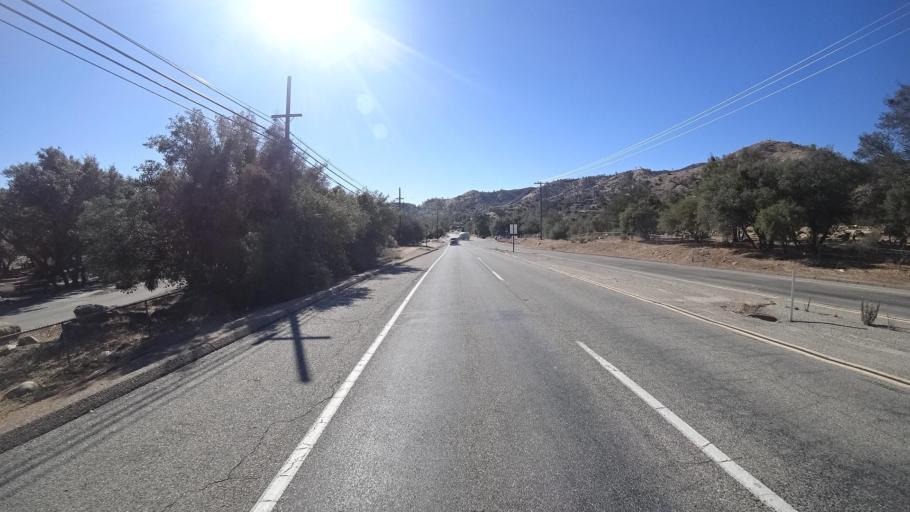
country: US
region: California
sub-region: Kern County
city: Wofford Heights
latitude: 35.7025
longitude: -118.4589
